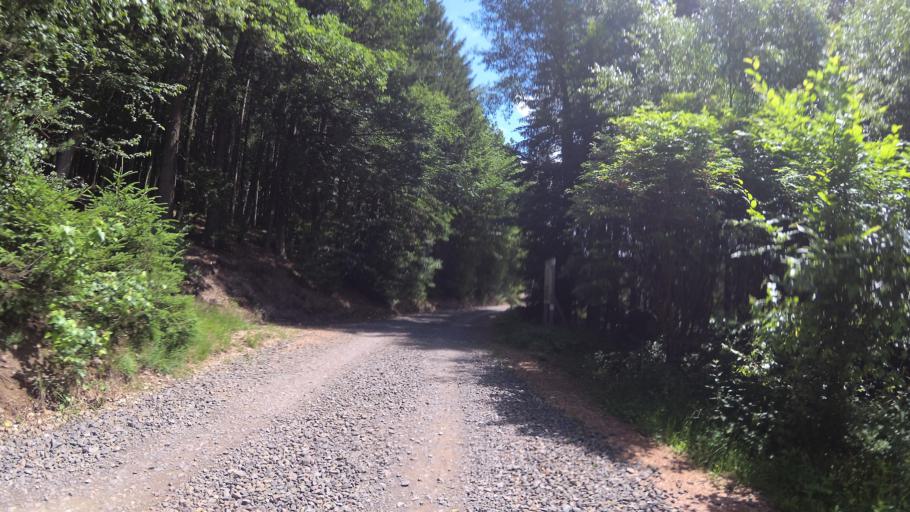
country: DE
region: Saarland
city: Oberthal
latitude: 49.5306
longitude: 7.0747
